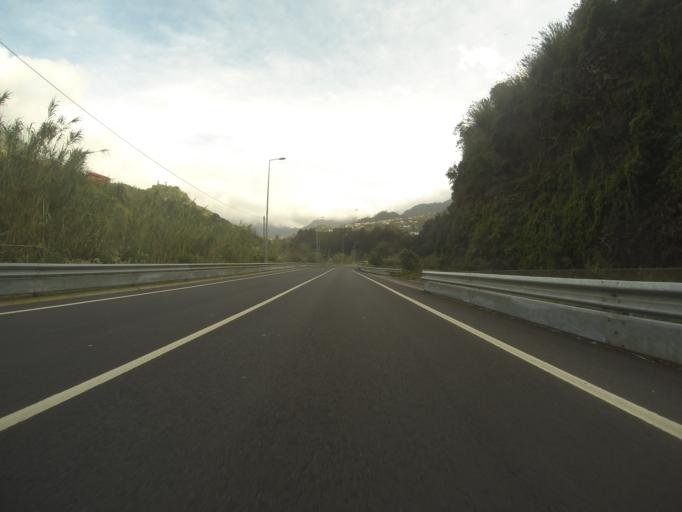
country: PT
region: Madeira
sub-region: Sao Vicente
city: Sao Vicente
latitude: 32.7999
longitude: -17.0430
